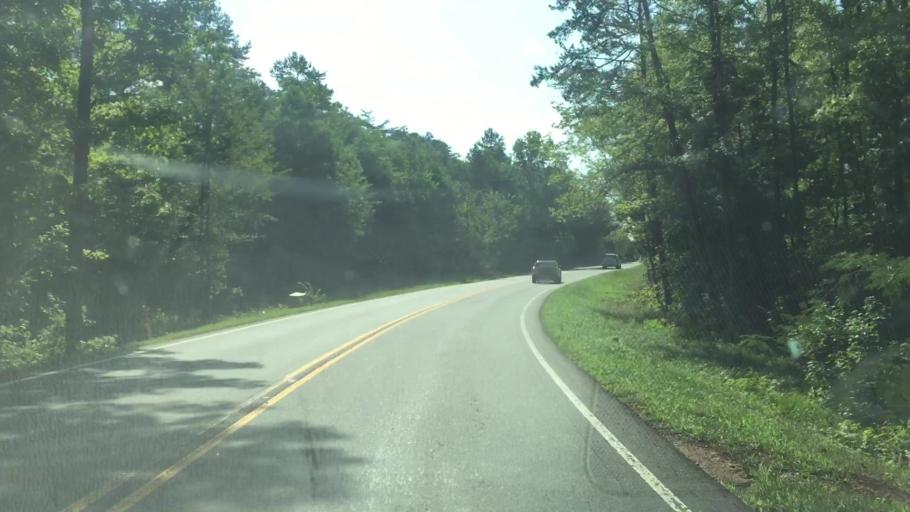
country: US
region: North Carolina
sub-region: Mecklenburg County
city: Mint Hill
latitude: 35.1717
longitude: -80.6066
